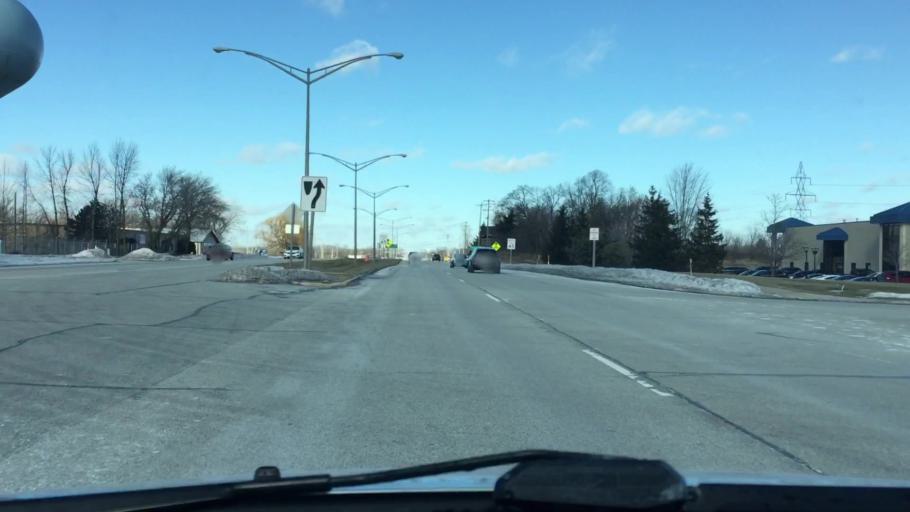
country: US
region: Wisconsin
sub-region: Milwaukee County
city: South Milwaukee
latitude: 42.9103
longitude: -87.9110
